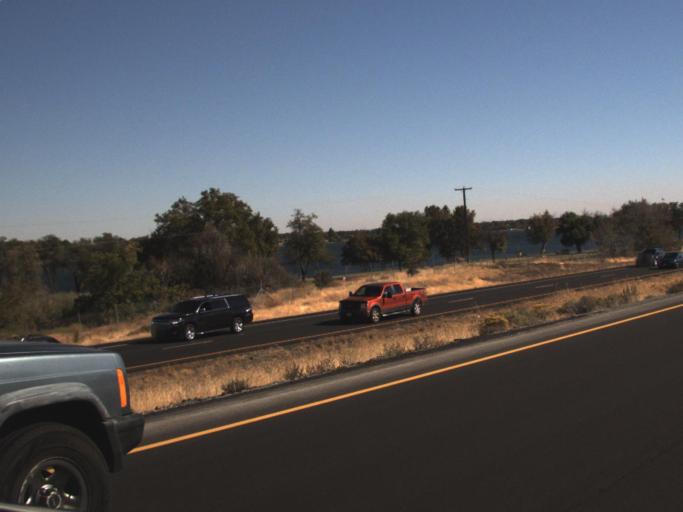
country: US
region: Washington
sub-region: Franklin County
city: West Pasco
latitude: 46.2244
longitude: -119.1706
